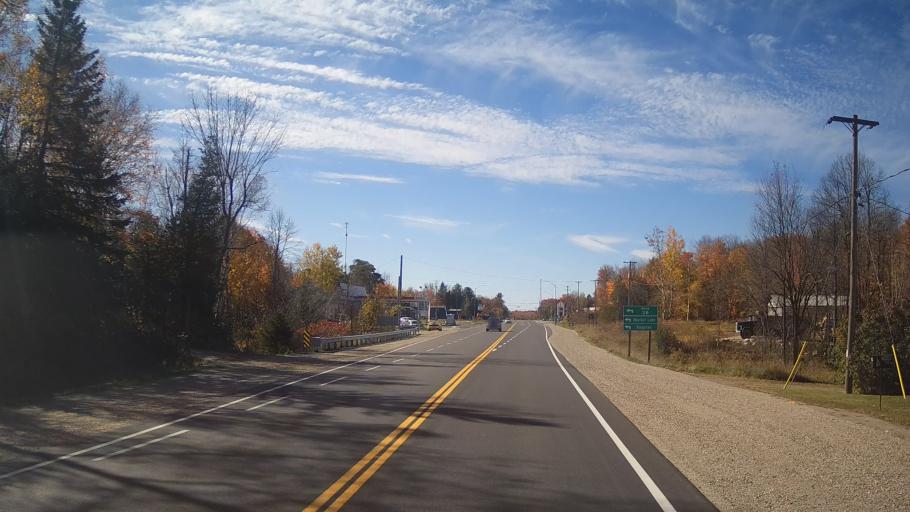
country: CA
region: Ontario
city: Perth
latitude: 44.7992
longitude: -76.6759
